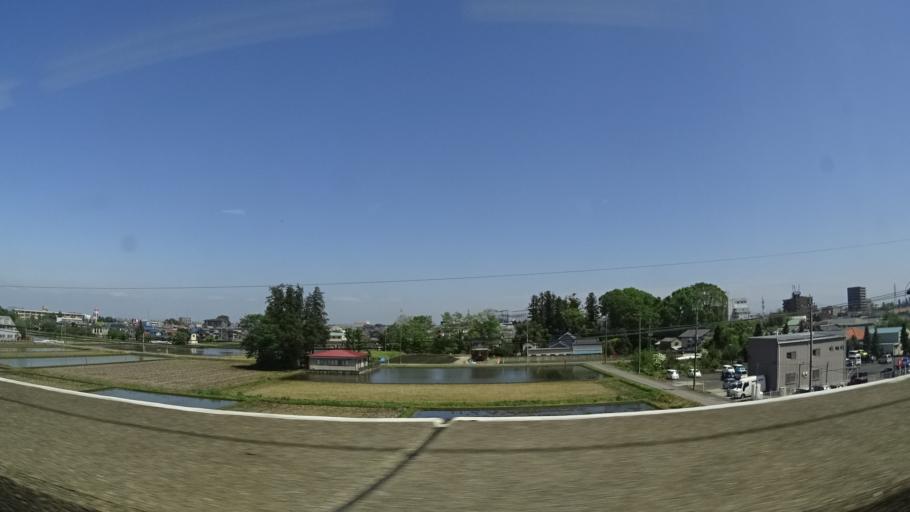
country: JP
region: Tochigi
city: Utsunomiya-shi
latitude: 36.5765
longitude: 139.9022
